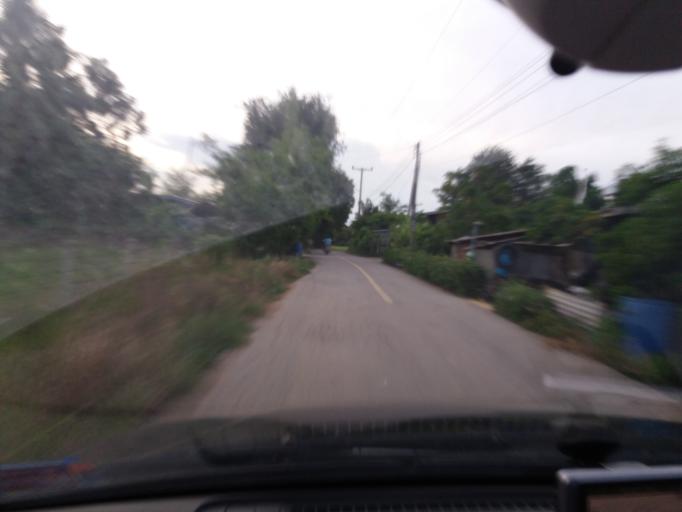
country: TH
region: Suphan Buri
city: Doembang Nangbuat
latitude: 14.8145
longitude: 100.1388
